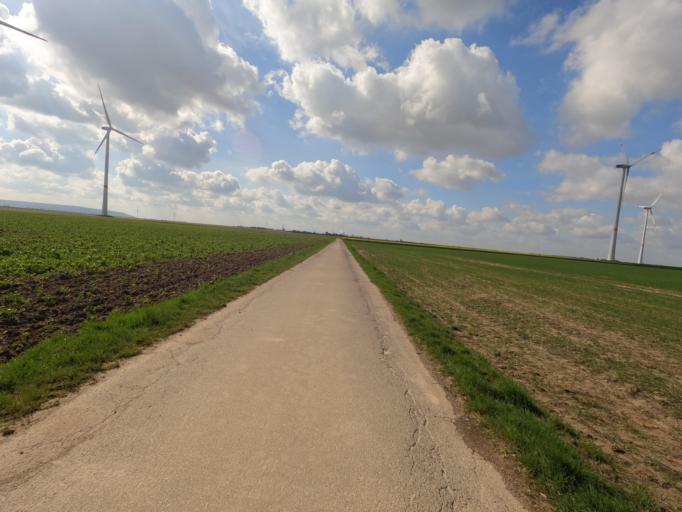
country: DE
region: North Rhine-Westphalia
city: Erkelenz
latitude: 51.0167
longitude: 6.3452
